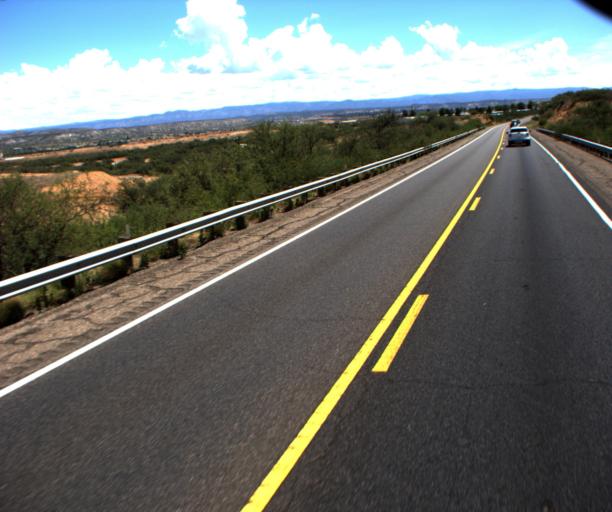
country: US
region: Arizona
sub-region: Yavapai County
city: Camp Verde
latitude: 34.6221
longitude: -111.9252
